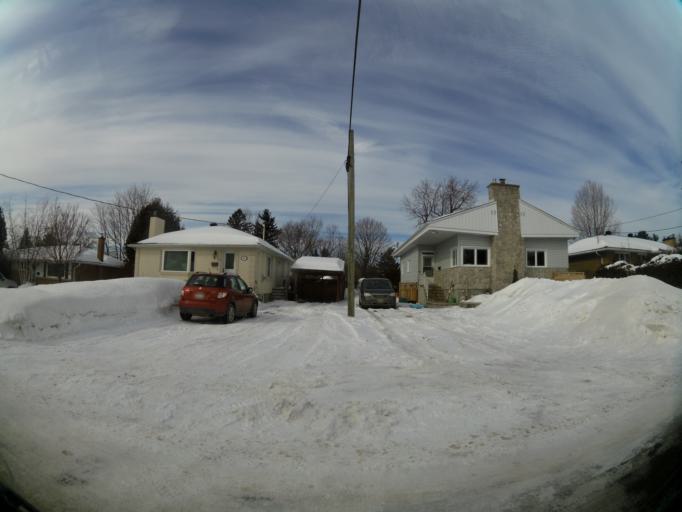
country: CA
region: Ontario
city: Ottawa
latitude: 45.4396
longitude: -75.6086
